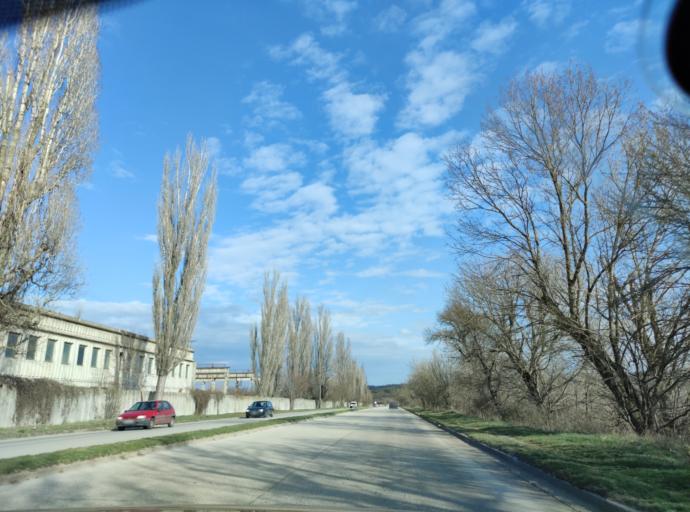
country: BG
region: Pleven
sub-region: Obshtina Dolna Mitropoliya
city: Dolna Mitropoliya
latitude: 43.4332
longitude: 24.5403
